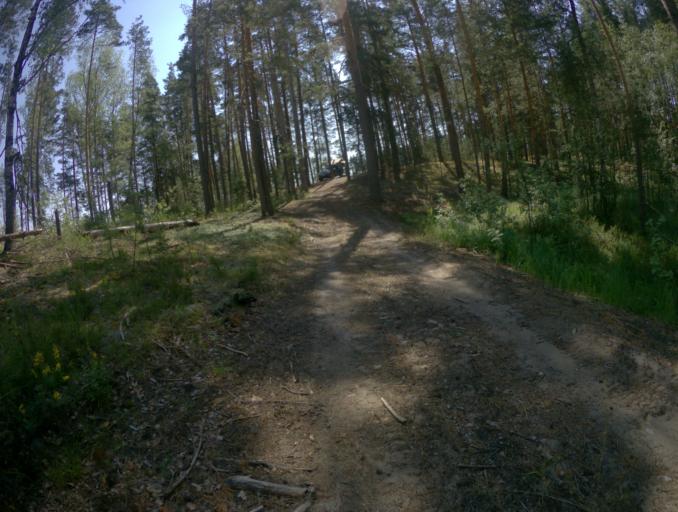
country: RU
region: Ivanovo
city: Talitsy
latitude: 56.4099
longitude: 42.2720
